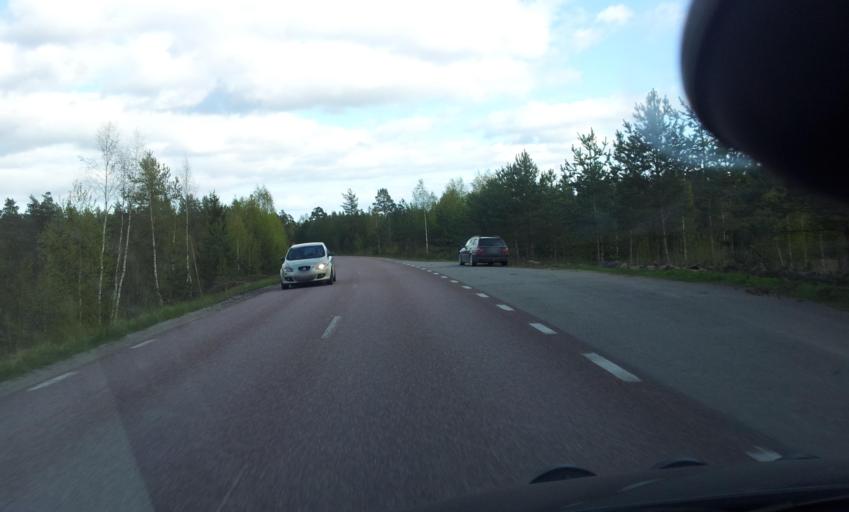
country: SE
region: Gaevleborg
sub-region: Bollnas Kommun
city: Kilafors
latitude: 61.3837
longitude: 16.6157
